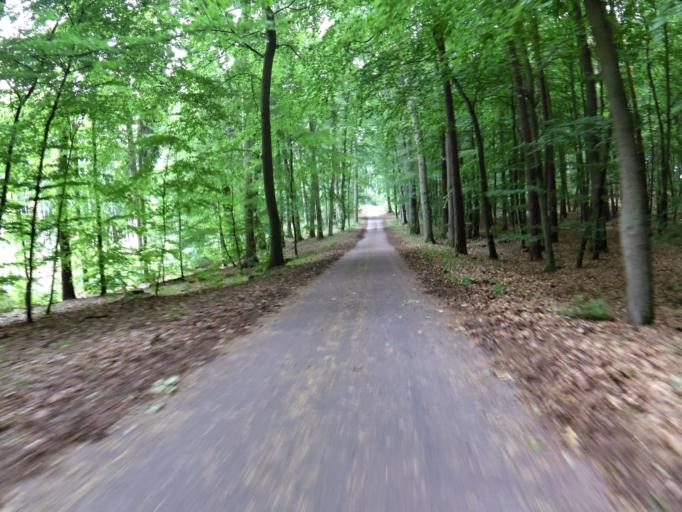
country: DE
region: Mecklenburg-Vorpommern
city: Seebad Heringsdorf
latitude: 53.9064
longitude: 14.1625
